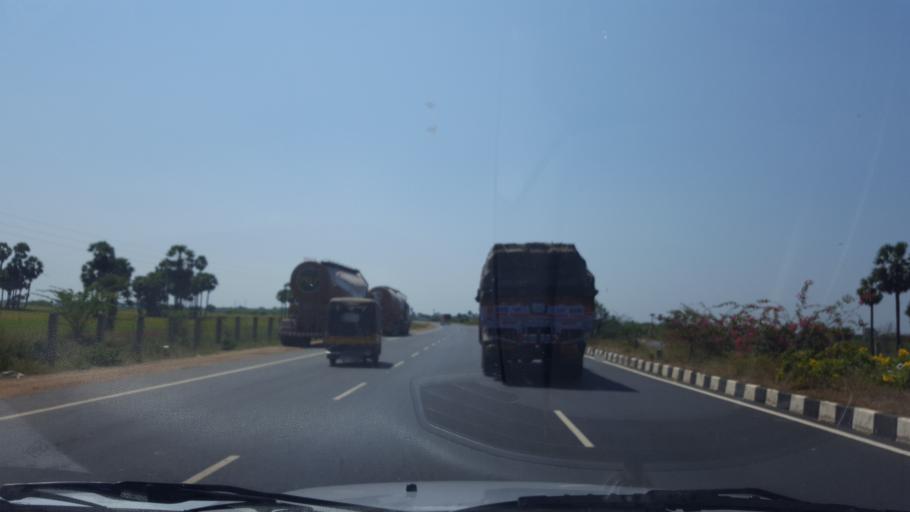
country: IN
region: Andhra Pradesh
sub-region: Nellore
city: Kavali
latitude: 14.8959
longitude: 80.0015
